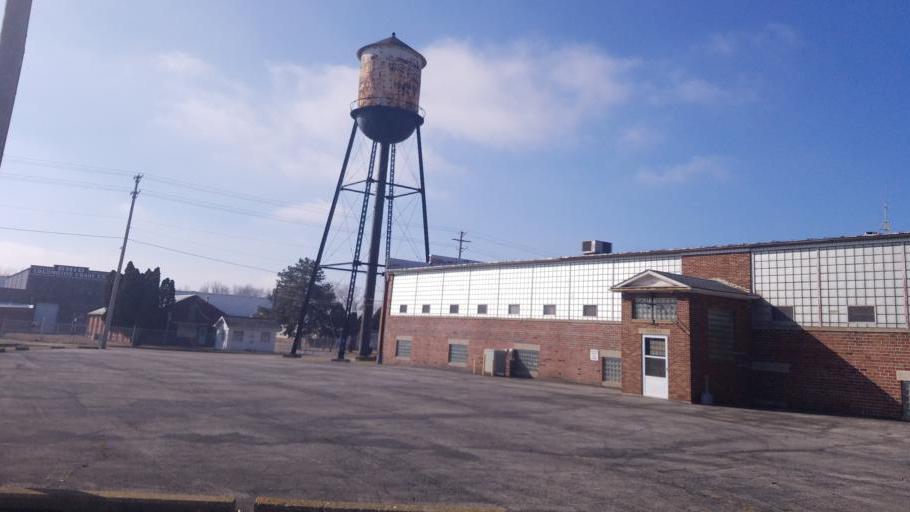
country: US
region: Ohio
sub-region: Crawford County
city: Bucyrus
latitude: 40.7984
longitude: -82.9652
